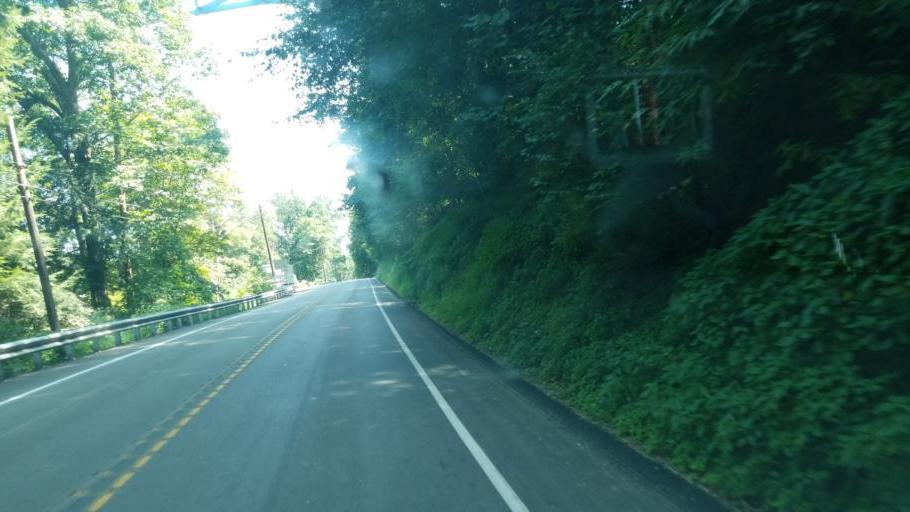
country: US
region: Pennsylvania
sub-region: Clarion County
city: Knox
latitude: 41.1741
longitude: -79.6992
